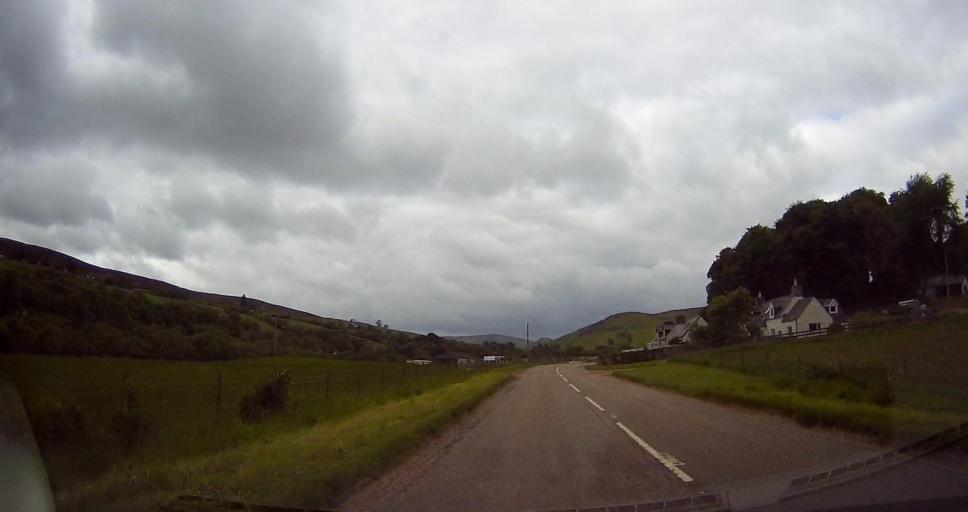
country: GB
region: Scotland
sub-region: Highland
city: Dornoch
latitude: 58.0035
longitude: -4.1977
